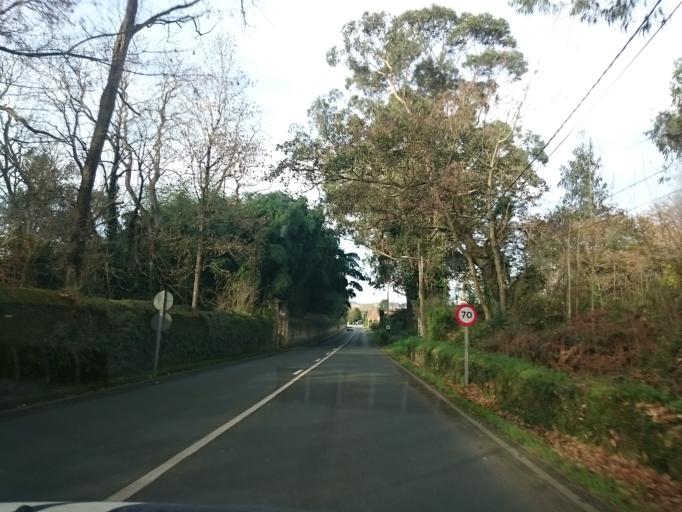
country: ES
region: Asturias
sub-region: Province of Asturias
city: Gijon
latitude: 43.5143
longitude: -5.6182
